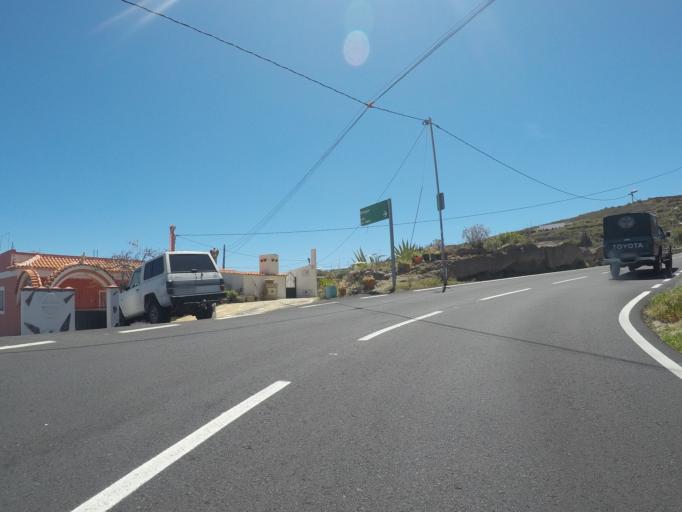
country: ES
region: Canary Islands
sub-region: Provincia de Santa Cruz de Tenerife
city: Lomo de Arico
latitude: 28.1733
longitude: -16.4918
